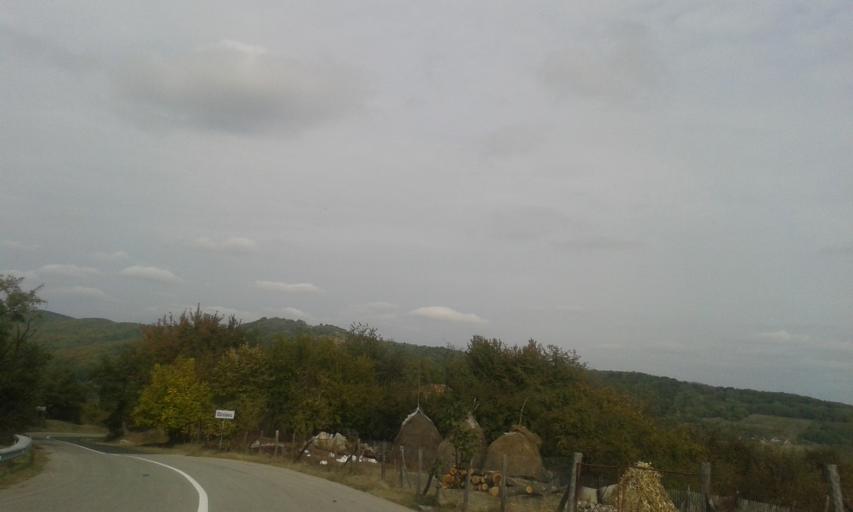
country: RO
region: Gorj
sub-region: Comuna Stejari
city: Piscoiu
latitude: 44.9142
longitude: 23.7712
